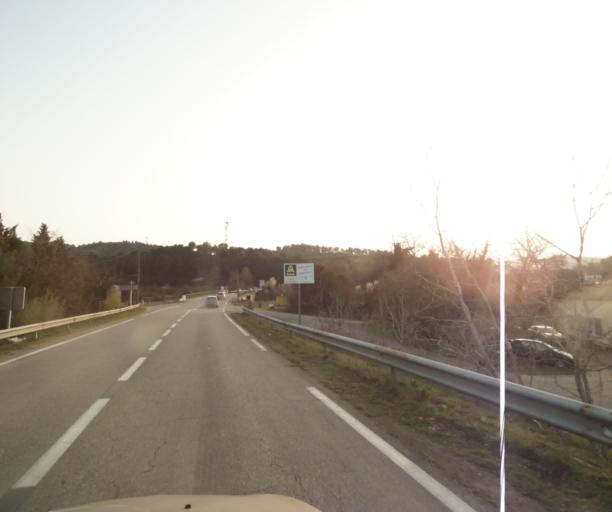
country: FR
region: Provence-Alpes-Cote d'Azur
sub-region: Departement du Vaucluse
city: Cadenet
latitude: 43.7097
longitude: 5.3646
